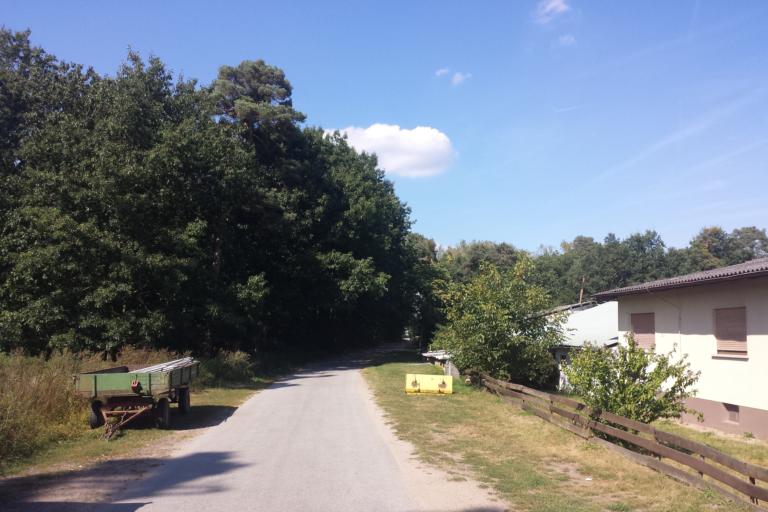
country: DE
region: Hesse
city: Lorsch
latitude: 49.6315
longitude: 8.5745
